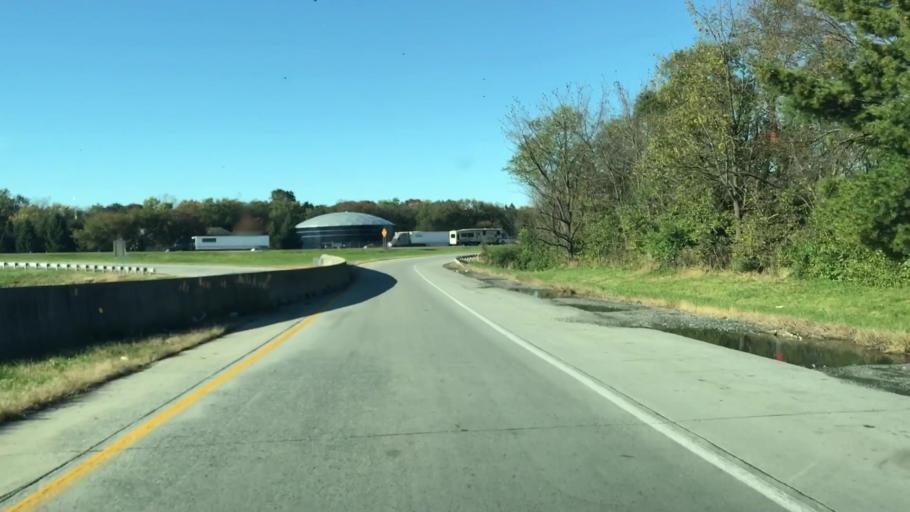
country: US
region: Pennsylvania
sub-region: Cumberland County
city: Schlusser
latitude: 40.2349
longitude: -77.1248
